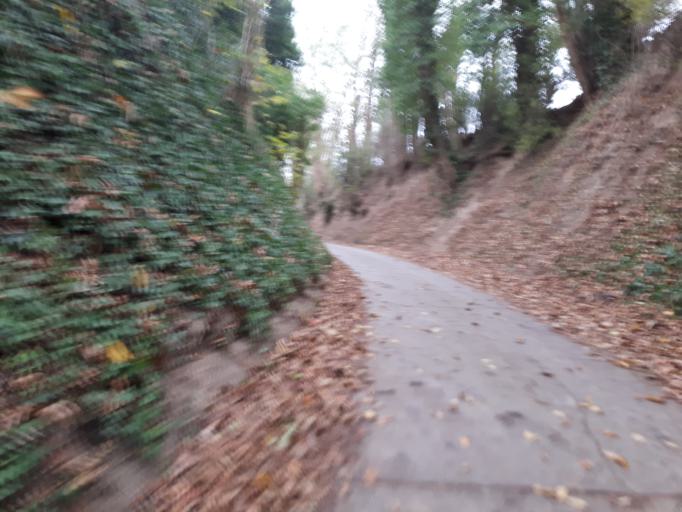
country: DE
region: Baden-Wuerttemberg
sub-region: Karlsruhe Region
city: Ostringen
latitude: 49.2093
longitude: 8.7200
